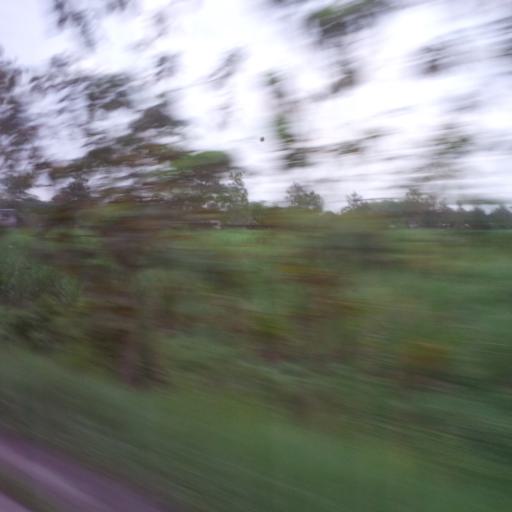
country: EC
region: Canar
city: La Troncal
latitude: -2.3419
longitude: -79.3779
